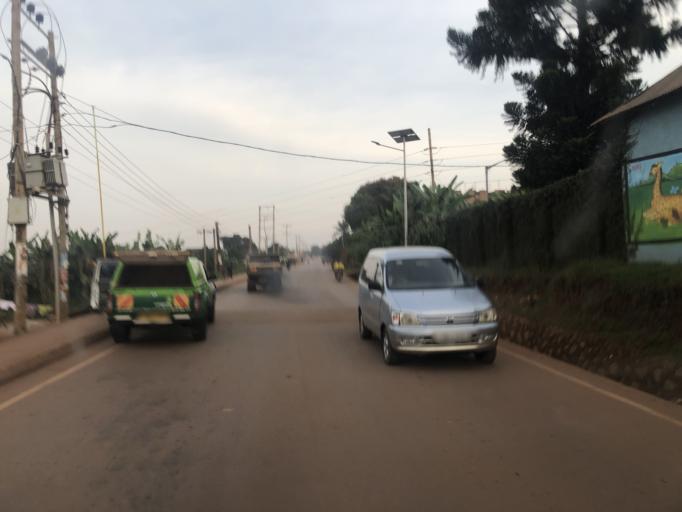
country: UG
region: Central Region
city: Kampala Central Division
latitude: 0.2893
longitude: 32.5366
